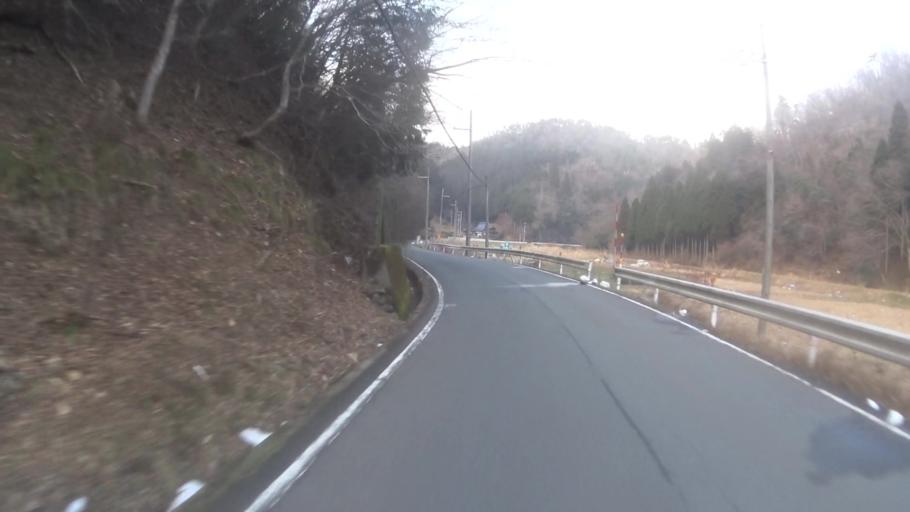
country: JP
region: Kyoto
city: Maizuru
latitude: 35.4154
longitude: 135.4631
